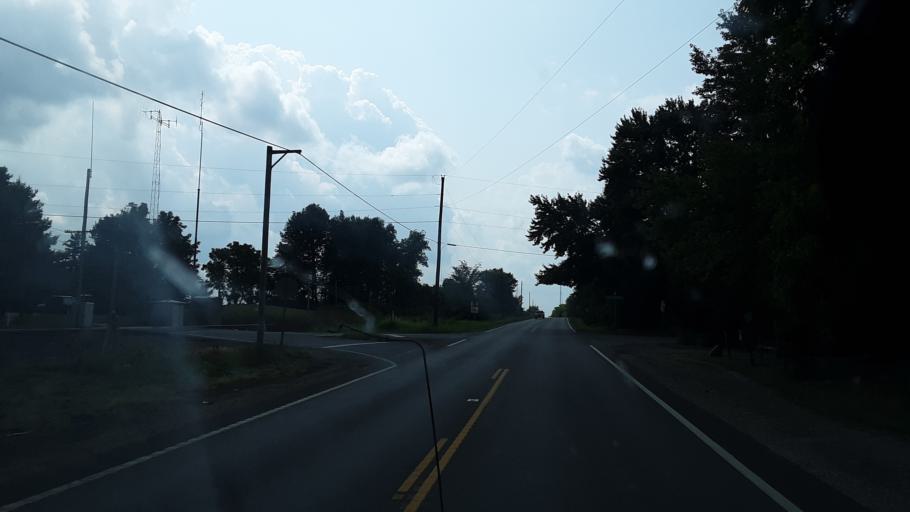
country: US
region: Ohio
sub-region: Delaware County
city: Ashley
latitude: 40.3578
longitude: -82.9885
